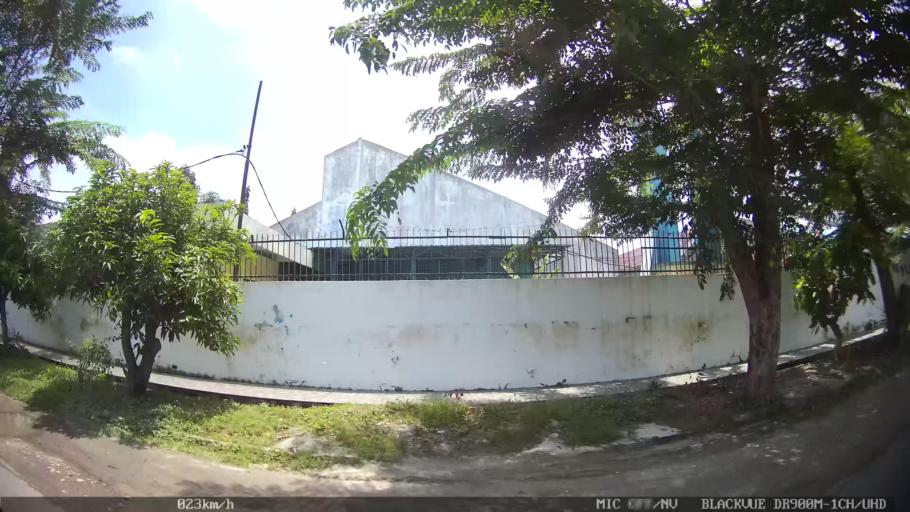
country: ID
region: North Sumatra
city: Perbaungan
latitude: 3.5422
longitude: 98.8794
